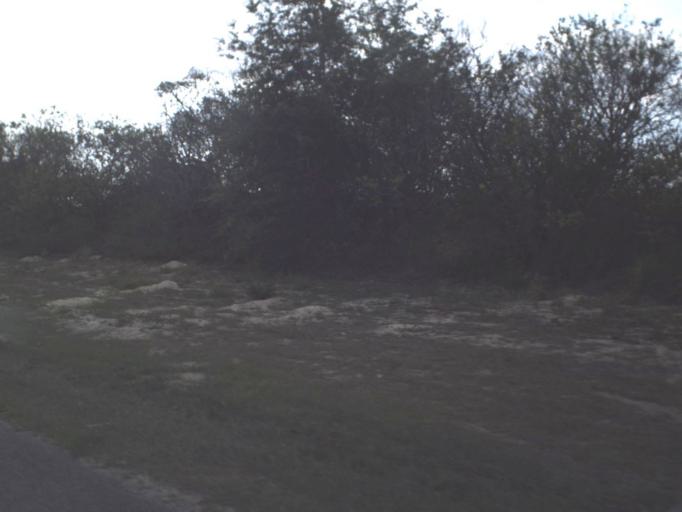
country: US
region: Florida
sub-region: Lake County
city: Mount Dora
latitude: 28.8006
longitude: -81.5999
